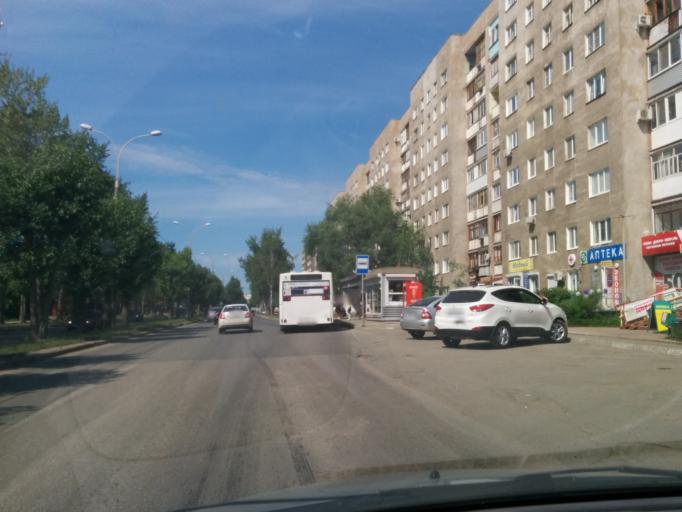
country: RU
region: Perm
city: Perm
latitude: 58.0109
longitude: 56.2940
